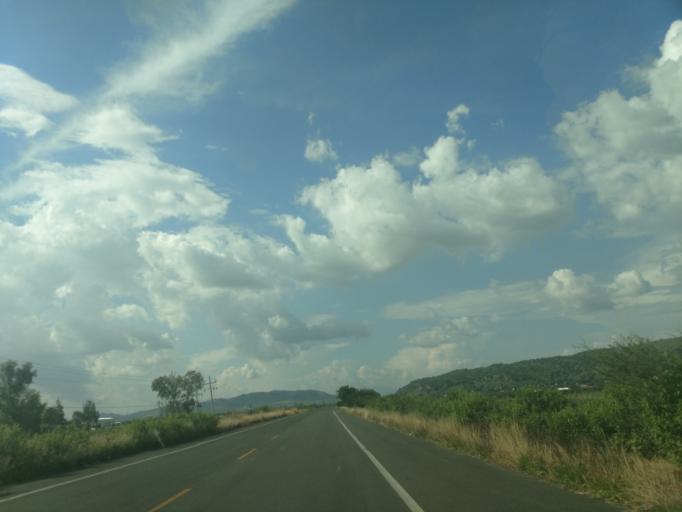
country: MX
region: Jalisco
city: Antonio Escobedo
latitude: 20.8966
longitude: -103.9943
